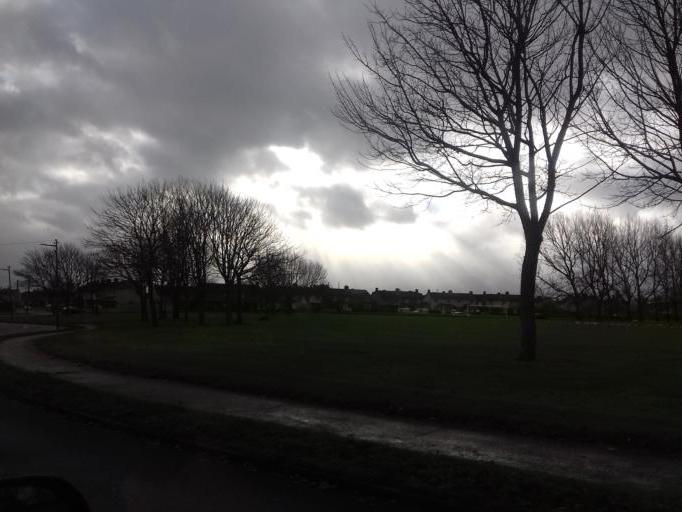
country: IE
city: Coolock
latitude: 53.3845
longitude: -6.1928
